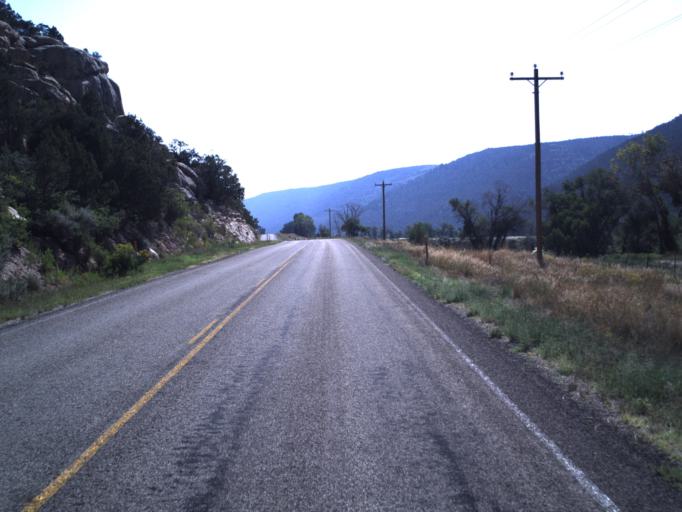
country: US
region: Utah
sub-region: Duchesne County
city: Duchesne
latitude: 40.3040
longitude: -110.6221
